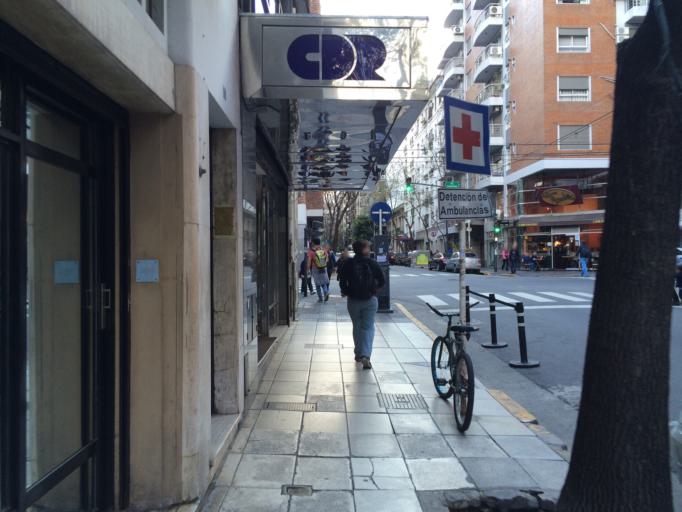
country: AR
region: Buenos Aires F.D.
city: Retiro
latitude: -34.5916
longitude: -58.4049
